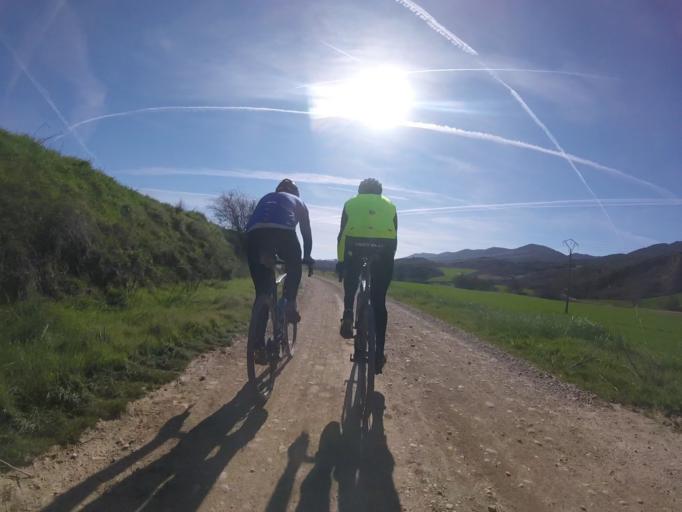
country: ES
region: Navarre
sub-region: Provincia de Navarra
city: Cirauqui
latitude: 42.6671
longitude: -1.9036
